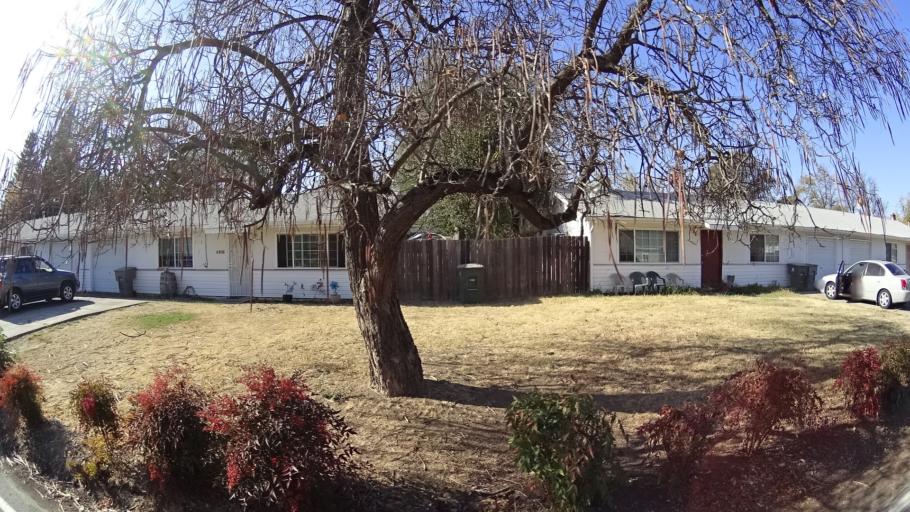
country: US
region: California
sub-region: Sacramento County
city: Citrus Heights
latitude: 38.7213
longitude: -121.2814
